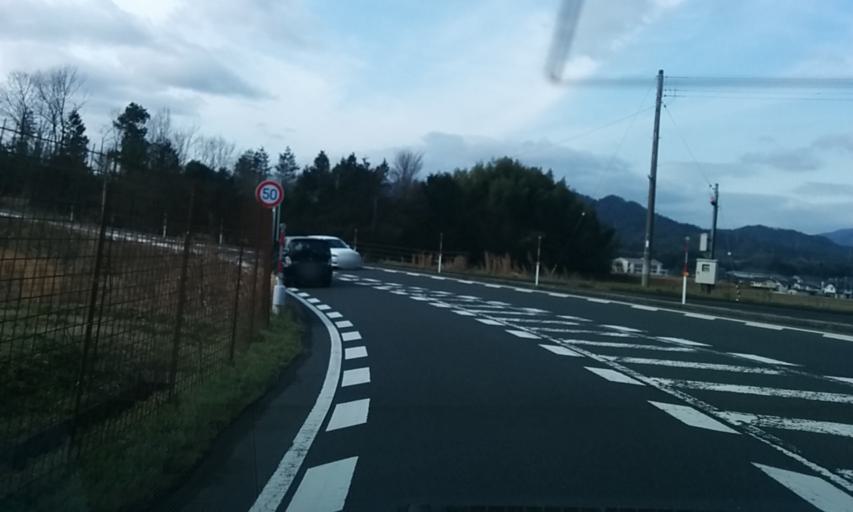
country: JP
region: Kyoto
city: Miyazu
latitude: 35.5835
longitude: 135.1059
